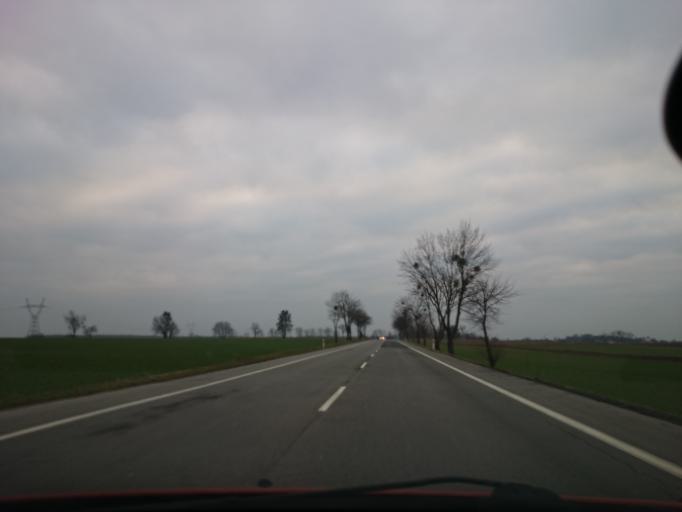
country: PL
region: Opole Voivodeship
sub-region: Powiat nyski
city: Lambinowice
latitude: 50.6020
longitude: 17.5428
